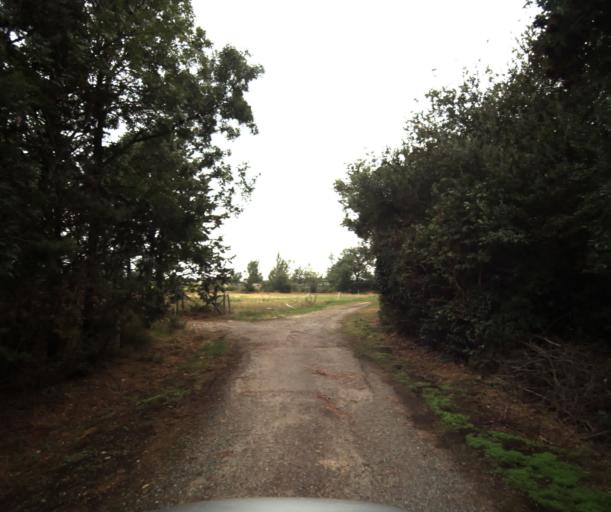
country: FR
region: Midi-Pyrenees
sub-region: Departement de la Haute-Garonne
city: Seysses
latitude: 43.4505
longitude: 1.3047
